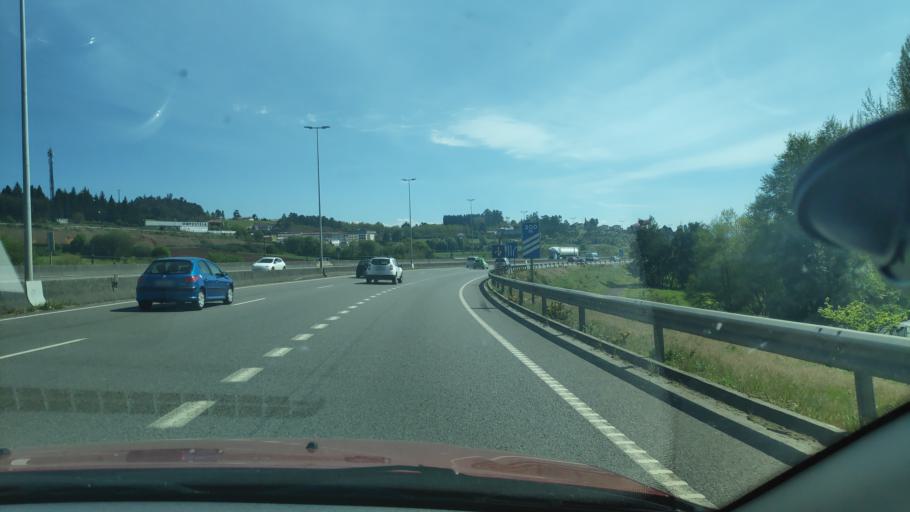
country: ES
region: Galicia
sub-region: Provincia da Coruna
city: Santiago de Compostela
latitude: 42.8948
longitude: -8.5072
